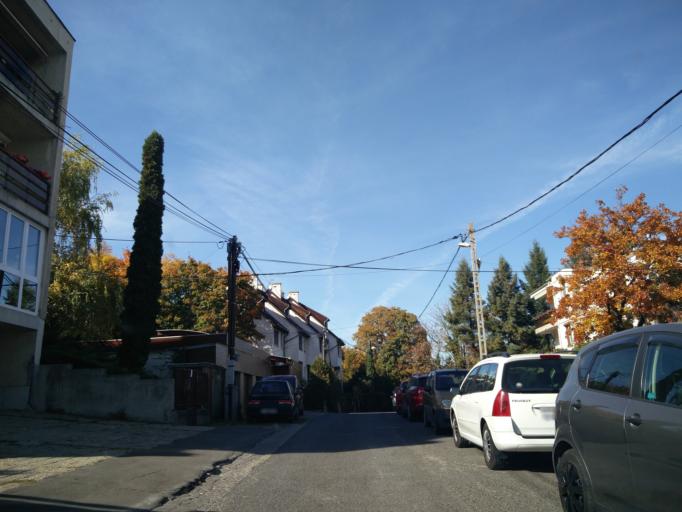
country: HU
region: Budapest
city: Budapest XII. keruelet
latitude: 47.5079
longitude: 18.9892
